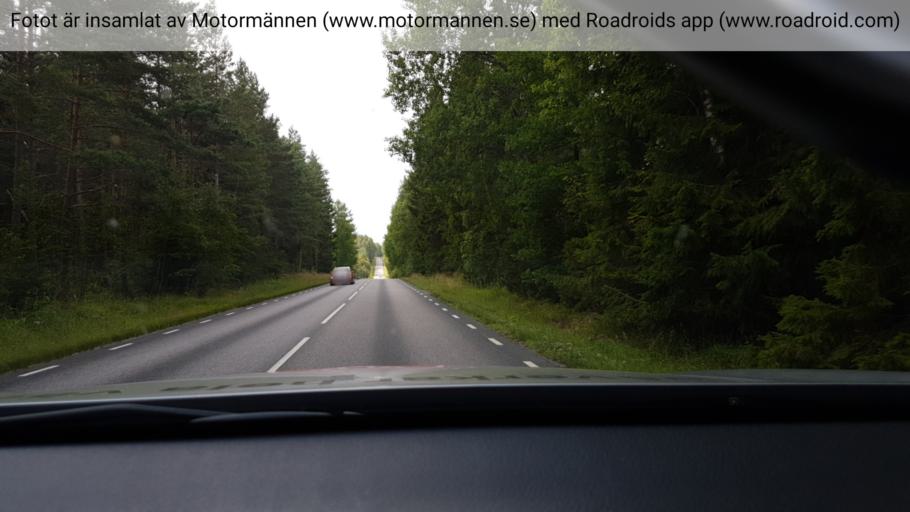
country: SE
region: Stockholm
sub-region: Norrtalje Kommun
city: Rimbo
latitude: 59.7105
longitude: 18.4258
